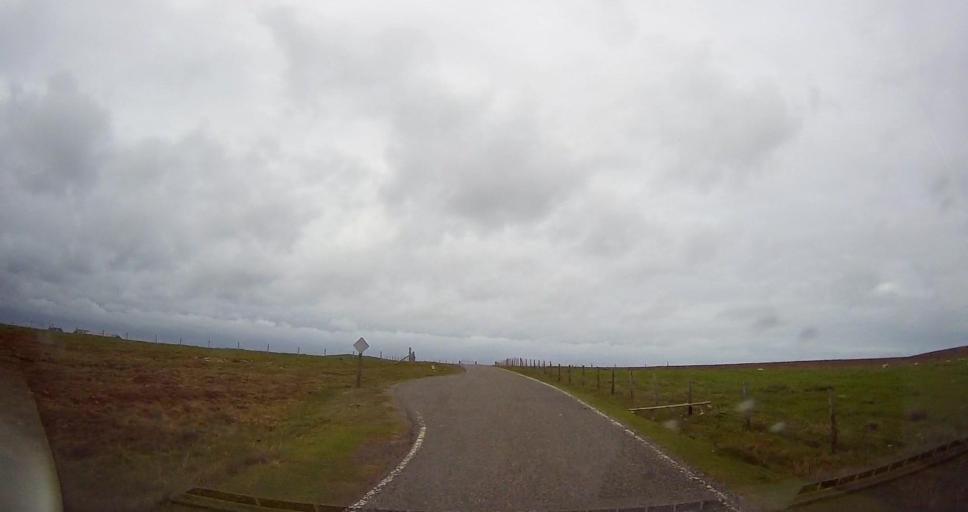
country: GB
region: Scotland
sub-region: Shetland Islands
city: Lerwick
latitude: 60.4893
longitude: -1.5930
